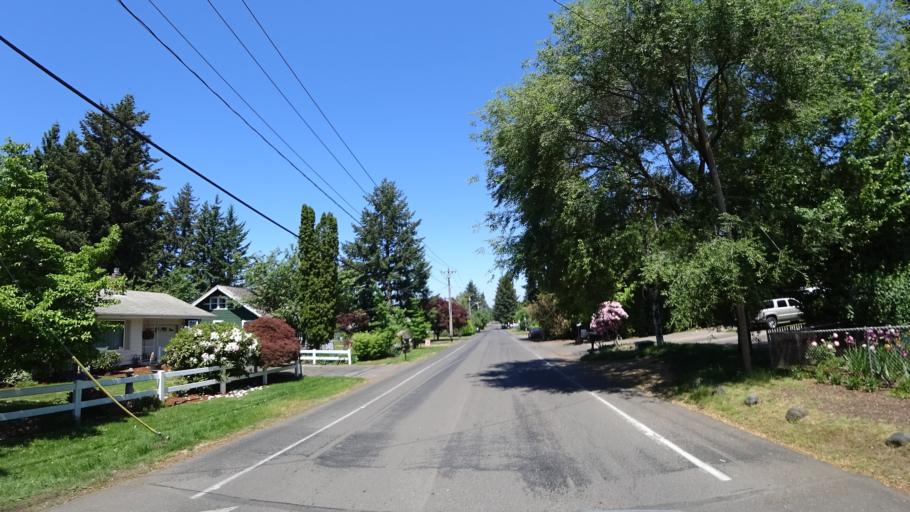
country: US
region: Oregon
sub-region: Clackamas County
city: Happy Valley
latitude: 45.4775
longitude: -122.5322
